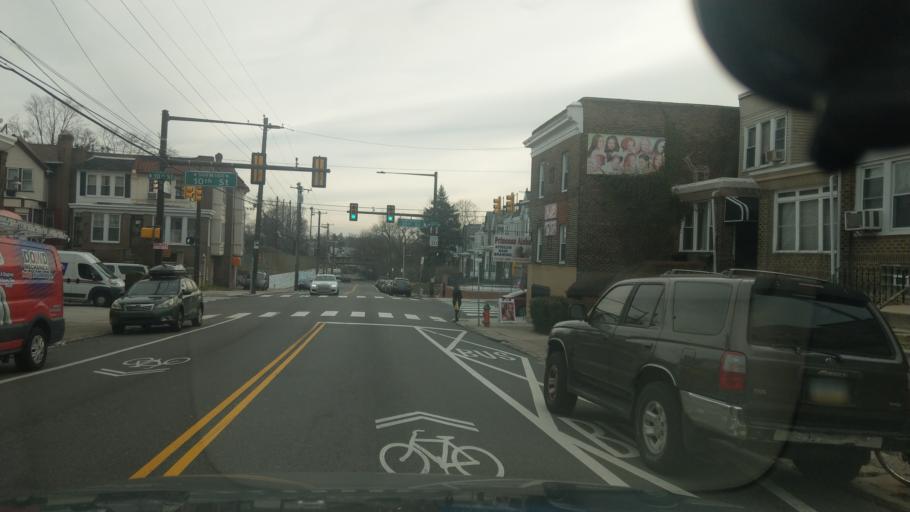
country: US
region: Pennsylvania
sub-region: Montgomery County
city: Wyncote
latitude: 40.0376
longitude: -75.1384
